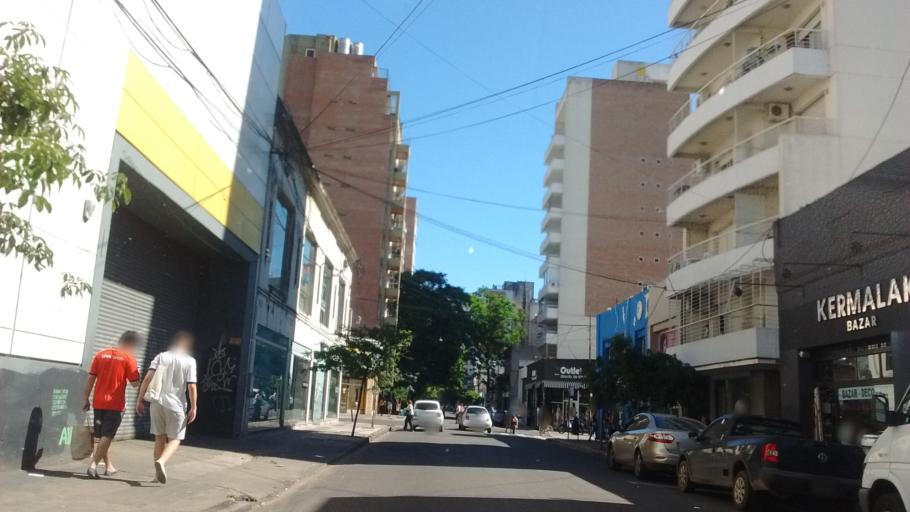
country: AR
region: Santa Fe
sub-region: Departamento de Rosario
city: Rosario
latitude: -32.9465
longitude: -60.6498
